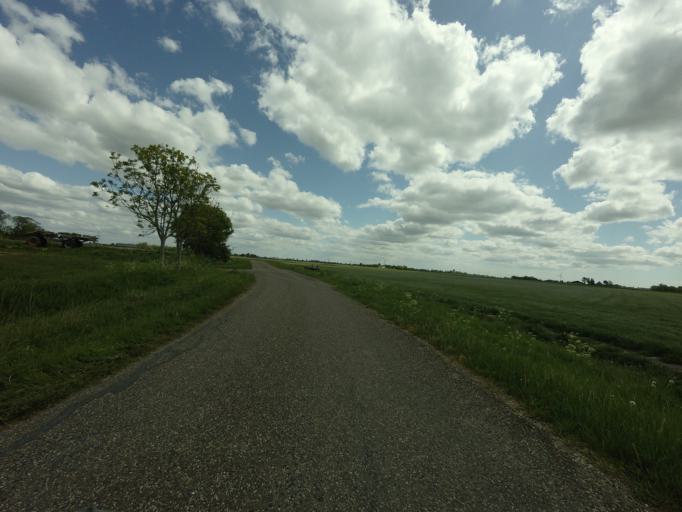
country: NL
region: Friesland
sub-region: Gemeente Franekeradeel
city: Tzum
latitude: 53.1343
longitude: 5.5631
